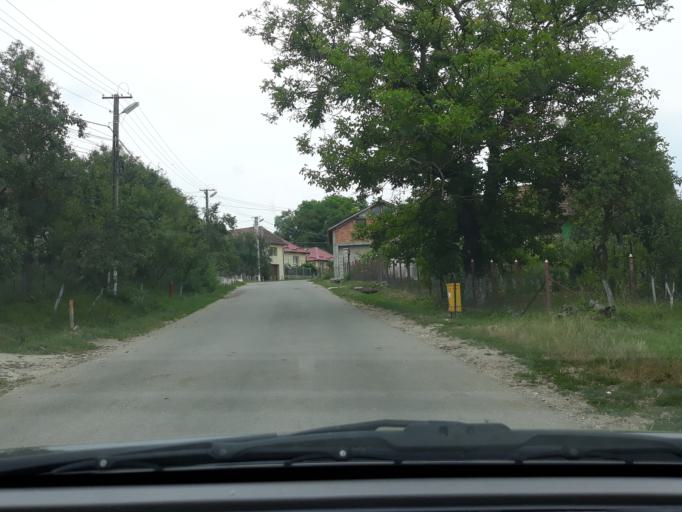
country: RO
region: Salaj
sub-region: Comuna Criseni
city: Criseni
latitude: 47.2554
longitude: 23.0635
